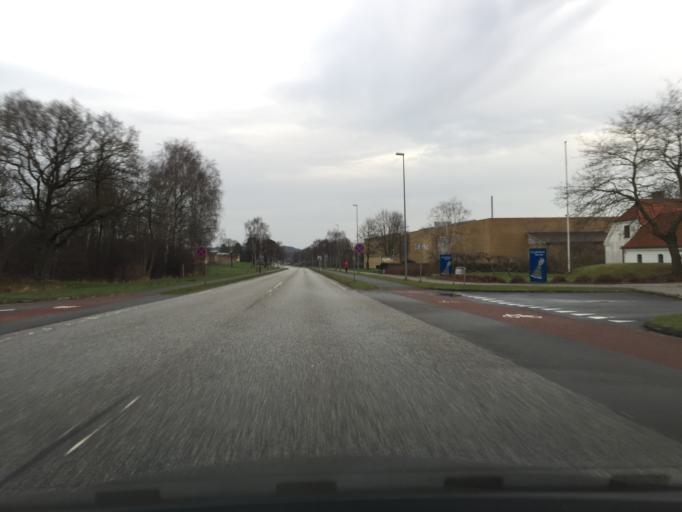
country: DK
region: Central Jutland
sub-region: Viborg Kommune
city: Bjerringbro
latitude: 56.3781
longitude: 9.6446
